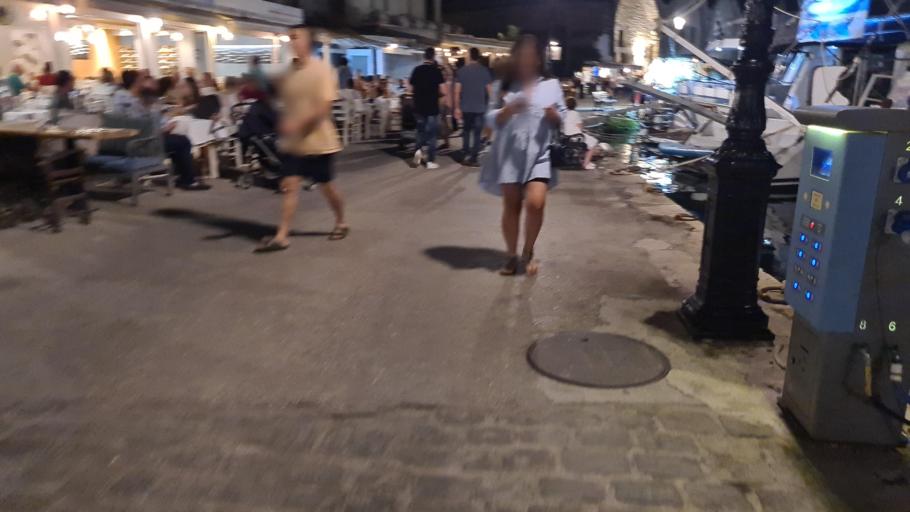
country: GR
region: Crete
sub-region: Nomos Chanias
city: Chania
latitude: 35.5185
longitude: 24.0225
